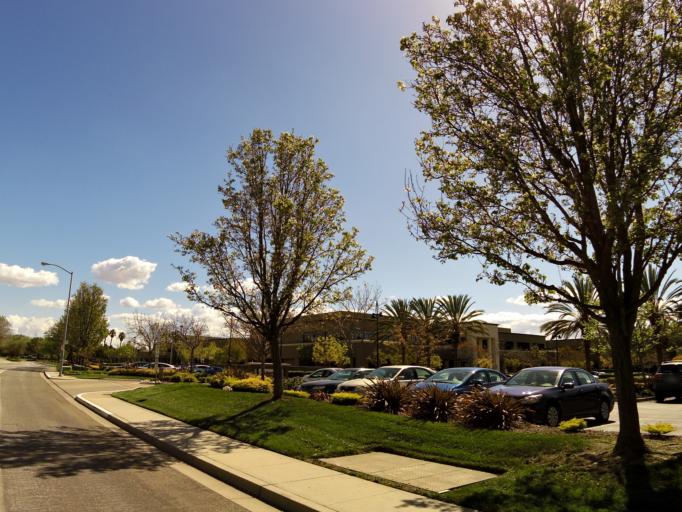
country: US
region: California
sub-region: Santa Clara County
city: Milpitas
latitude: 37.4803
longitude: -121.9407
